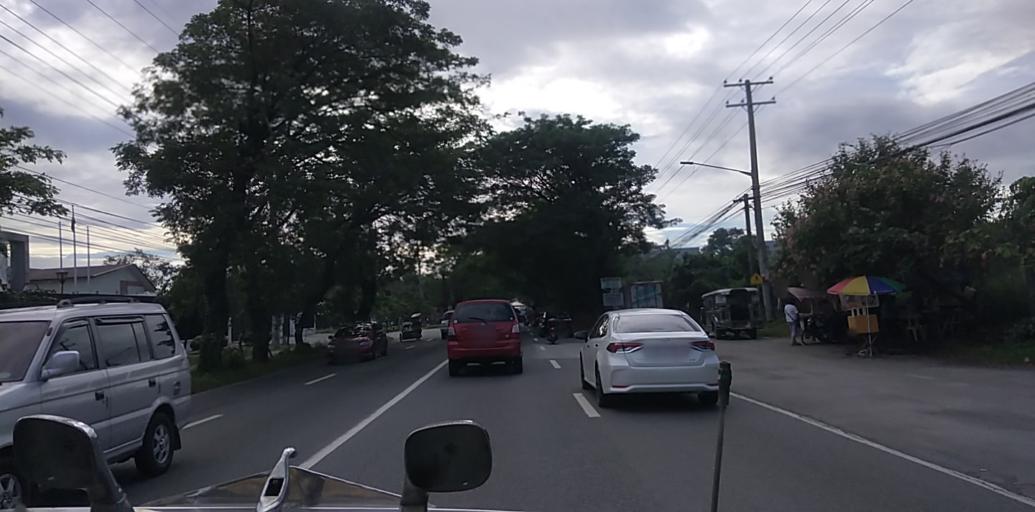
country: PH
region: Central Luzon
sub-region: Province of Pampanga
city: Bulaon
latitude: 15.0868
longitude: 120.6327
